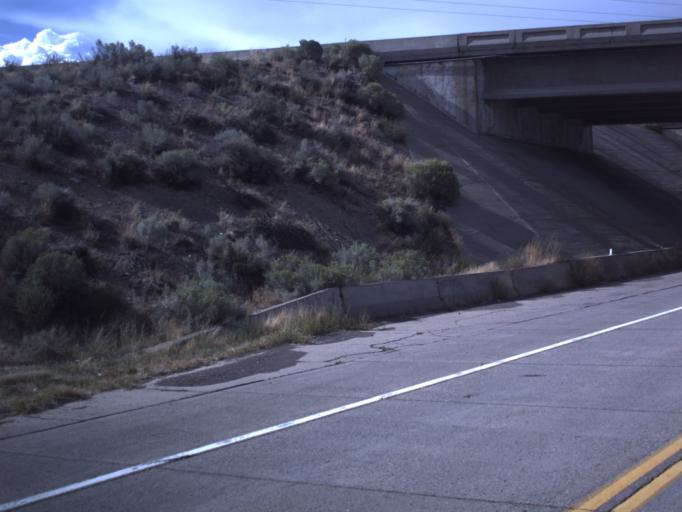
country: US
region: Utah
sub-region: Sevier County
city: Monroe
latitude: 38.5992
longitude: -112.2544
